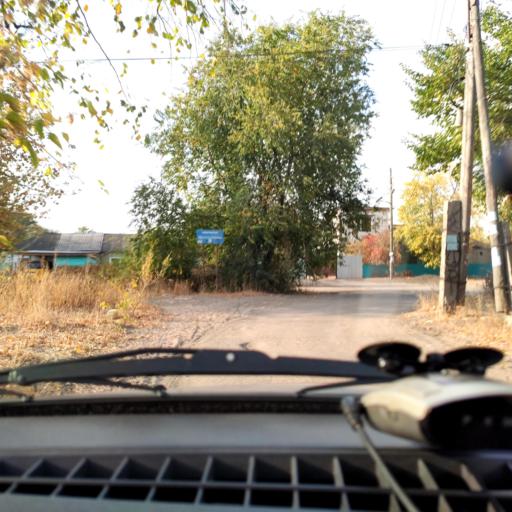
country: RU
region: Voronezj
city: Voronezh
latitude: 51.6539
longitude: 39.2371
